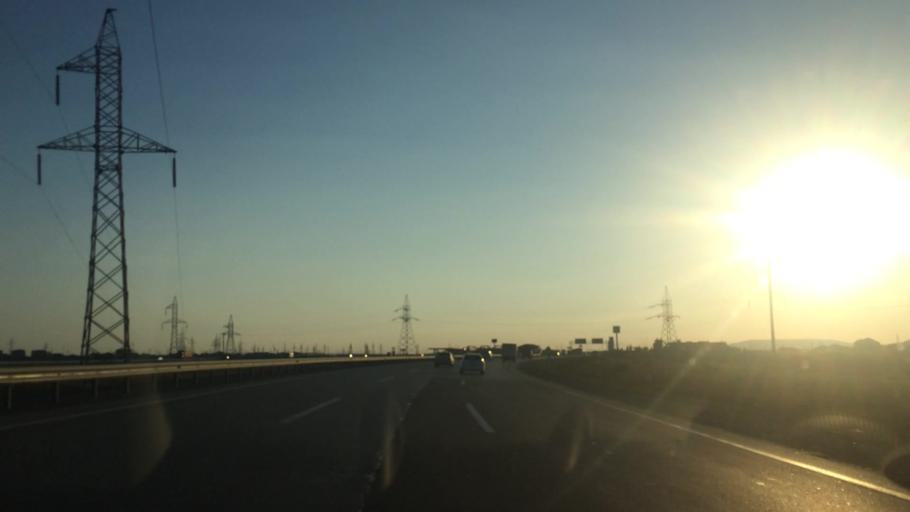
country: AZ
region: Baki
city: Qobustan
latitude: 39.9691
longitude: 49.4133
